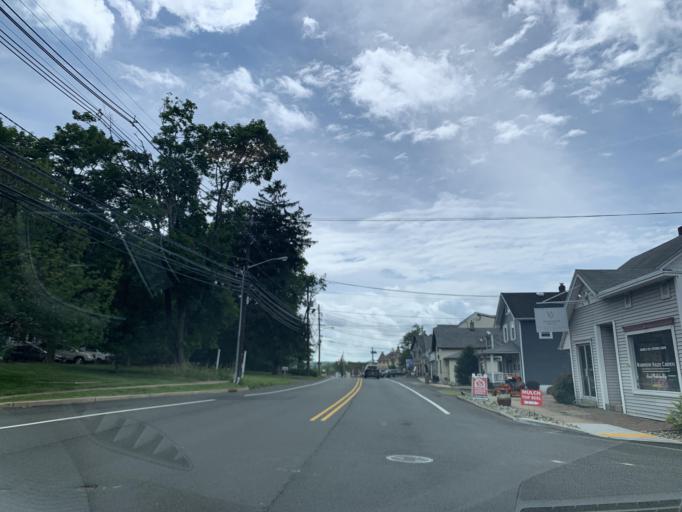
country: US
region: New Jersey
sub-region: Somerset County
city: Martinsville
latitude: 40.6022
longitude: -74.5632
